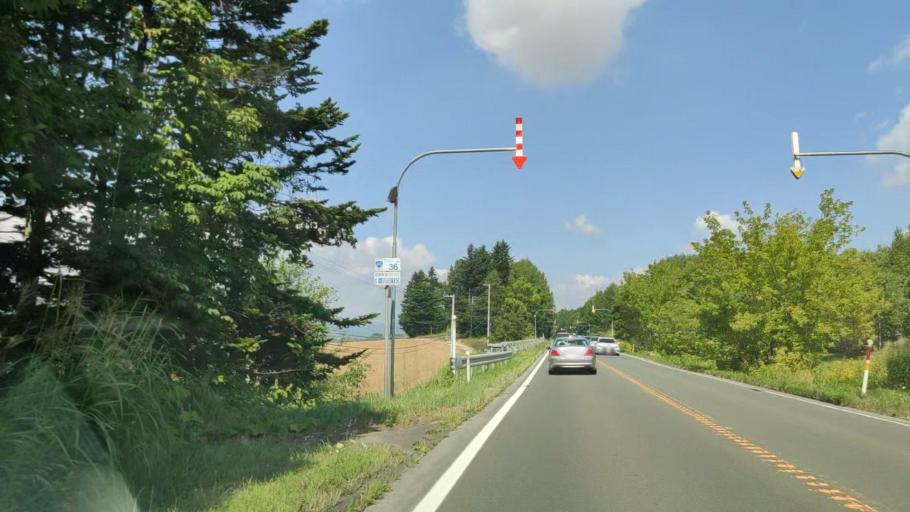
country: JP
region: Hokkaido
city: Shimo-furano
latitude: 43.5077
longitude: 142.4564
